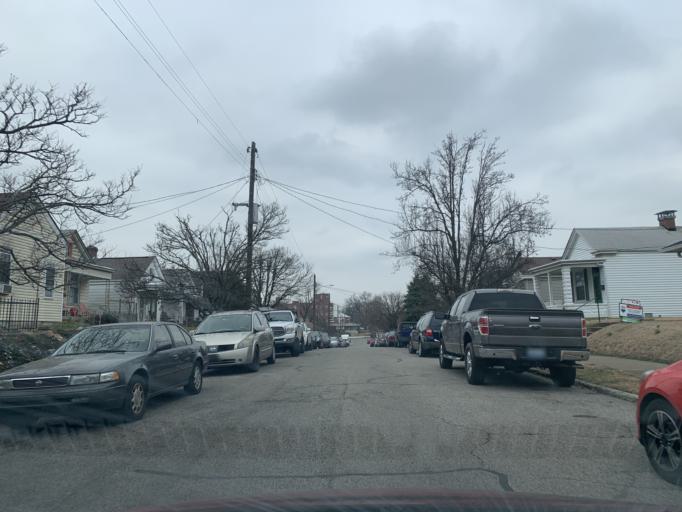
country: US
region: Kentucky
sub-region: Jefferson County
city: Audubon Park
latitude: 38.2258
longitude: -85.7396
